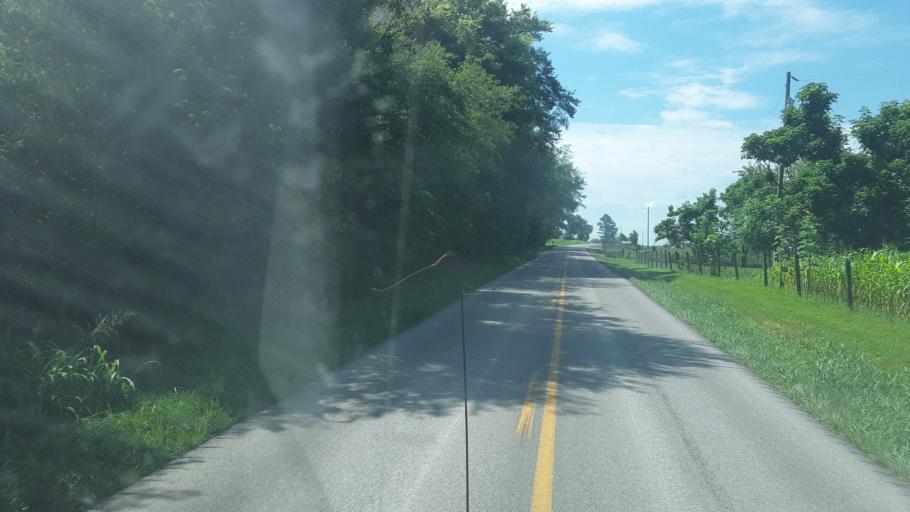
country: US
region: Kentucky
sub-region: Todd County
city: Elkton
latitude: 36.8141
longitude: -87.3142
